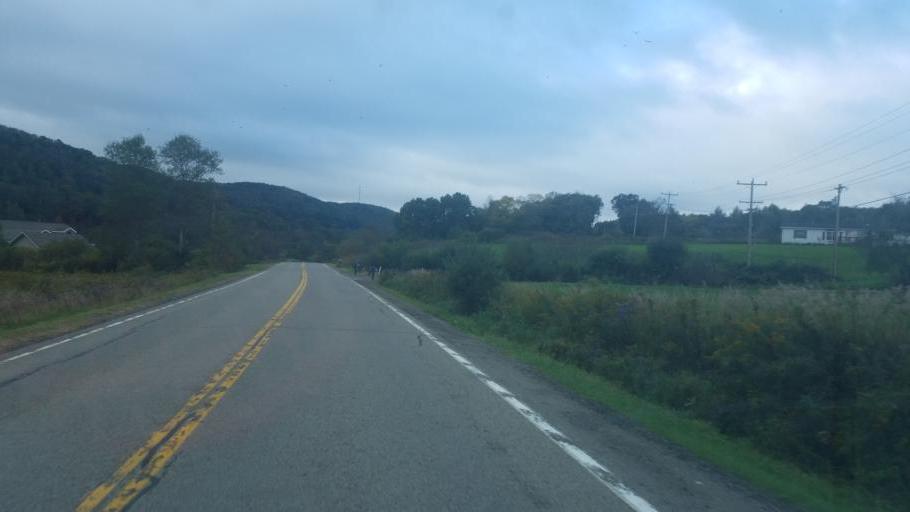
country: US
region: New York
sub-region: Allegany County
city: Cuba
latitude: 42.1846
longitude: -78.3585
